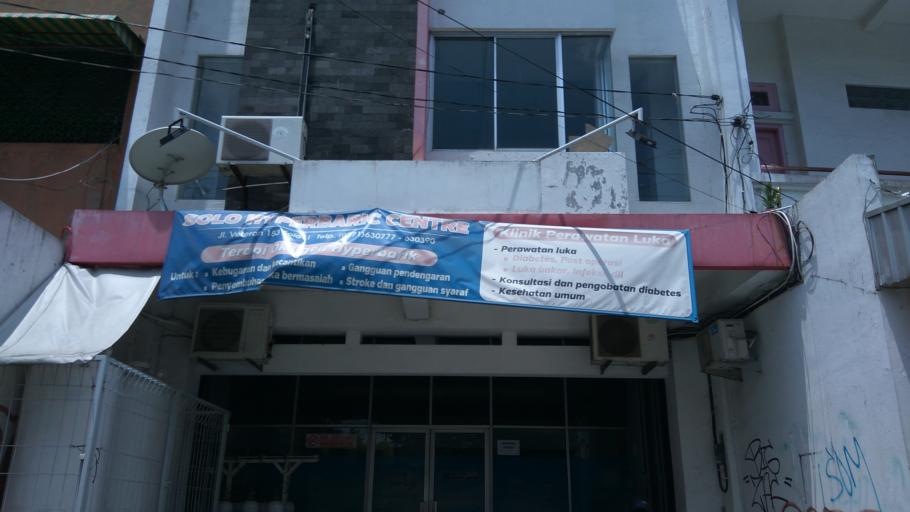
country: ID
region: Central Java
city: Grogol
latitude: -7.5827
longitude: 110.8225
